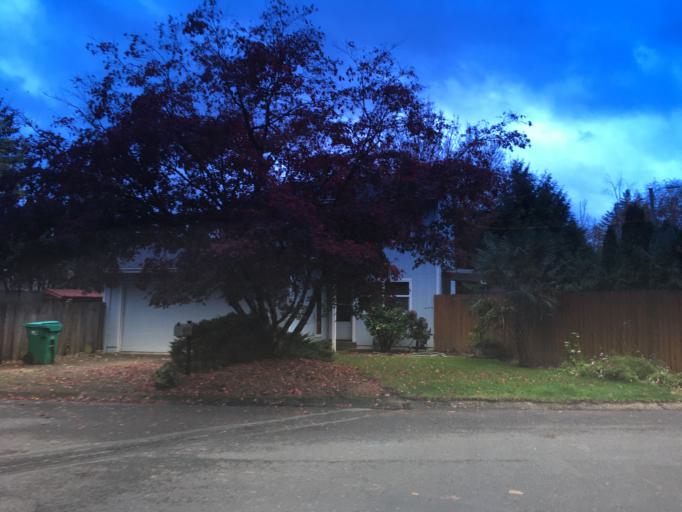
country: US
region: Oregon
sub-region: Multnomah County
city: Fairview
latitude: 45.5212
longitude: -122.4515
